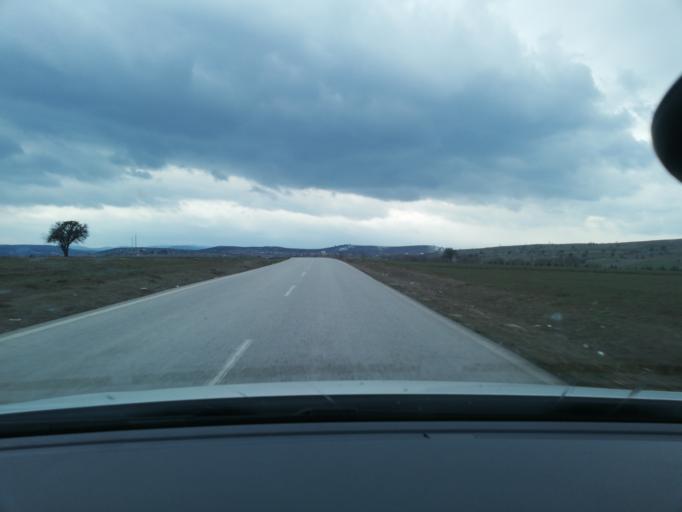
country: TR
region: Bolu
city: Gerede
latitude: 40.7052
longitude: 32.2253
